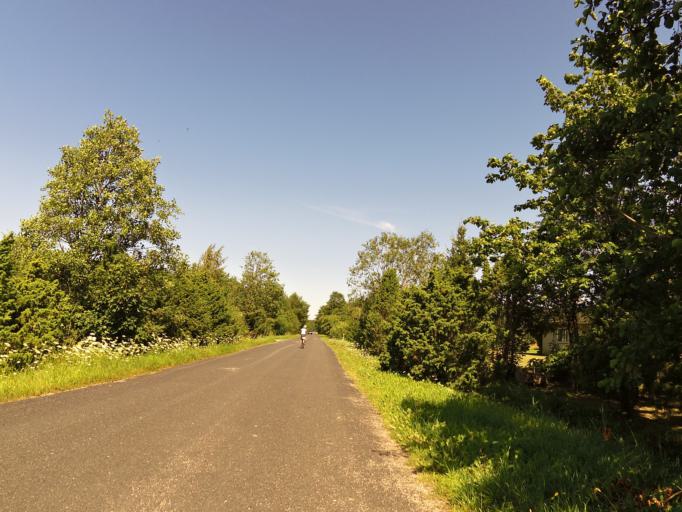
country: EE
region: Hiiumaa
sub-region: Kaerdla linn
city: Kardla
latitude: 58.7810
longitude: 22.4879
